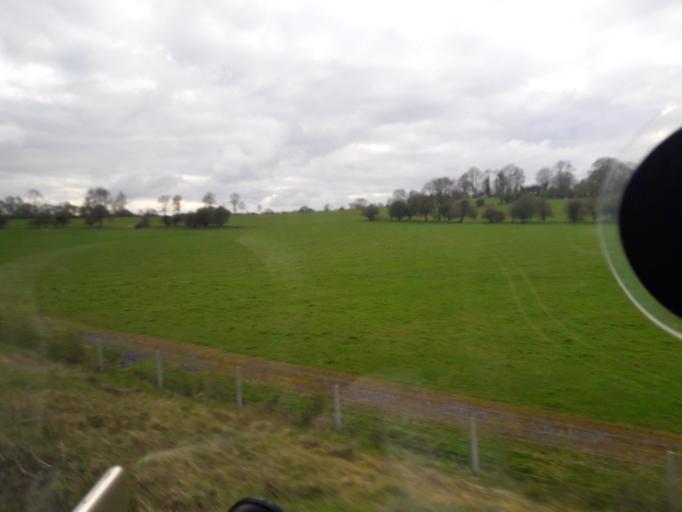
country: IE
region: Leinster
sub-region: An Iarmhi
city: An Muileann gCearr
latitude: 53.6249
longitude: -7.4160
